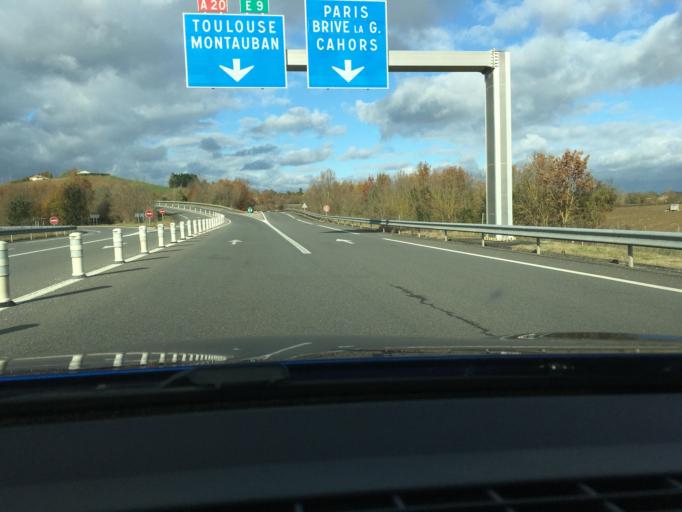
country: FR
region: Midi-Pyrenees
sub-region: Departement du Tarn-et-Garonne
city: Caussade
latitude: 44.1513
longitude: 1.5154
